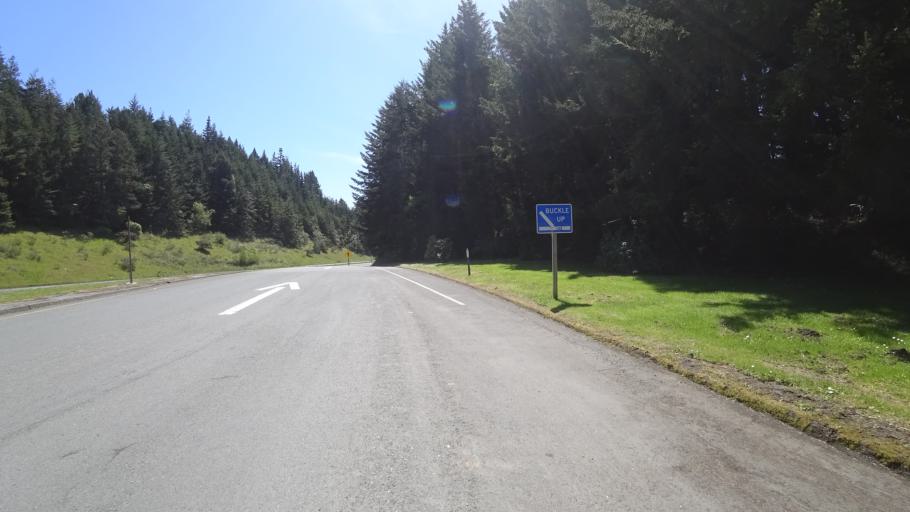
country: US
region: California
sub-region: Humboldt County
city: Westhaven-Moonstone
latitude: 41.0912
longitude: -124.1505
